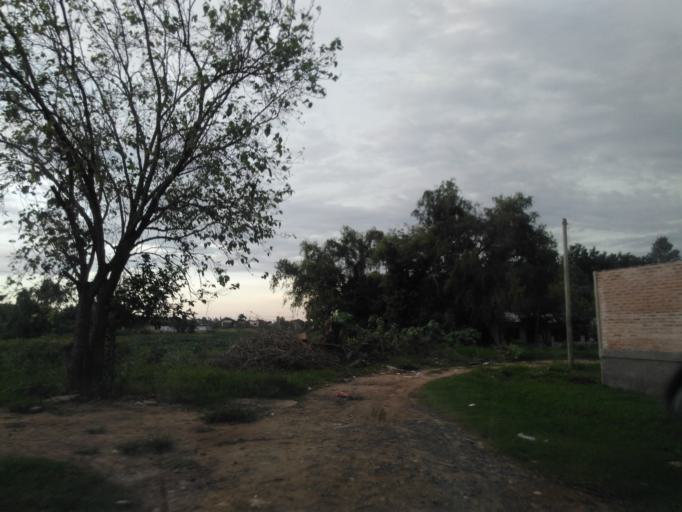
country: AR
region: Chaco
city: Resistencia
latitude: -27.4426
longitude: -58.9718
